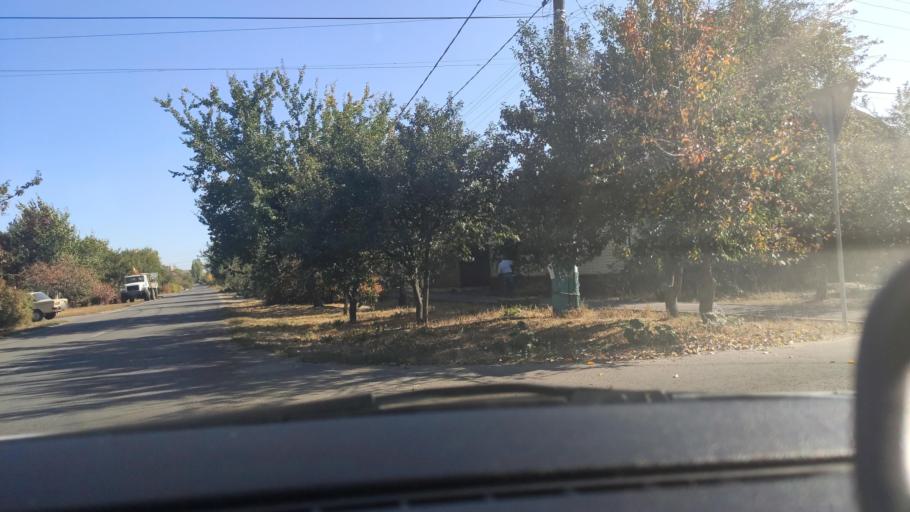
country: RU
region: Voronezj
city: Voronezh
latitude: 51.6661
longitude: 39.2601
